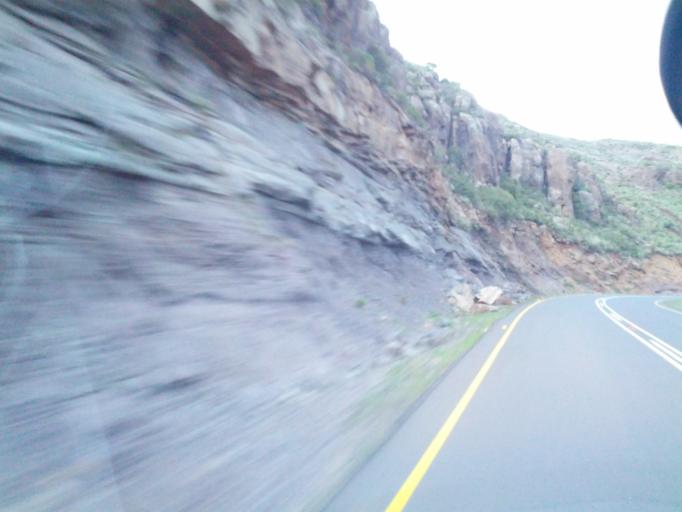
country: LS
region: Qacha's Nek
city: Qacha's Nek
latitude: -30.0380
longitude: 28.3063
